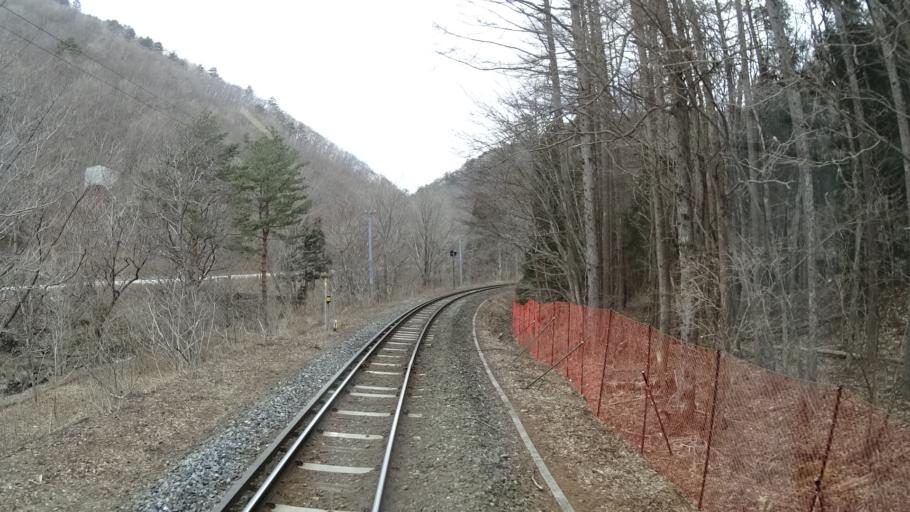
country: JP
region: Iwate
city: Tono
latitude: 39.2568
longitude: 141.6504
